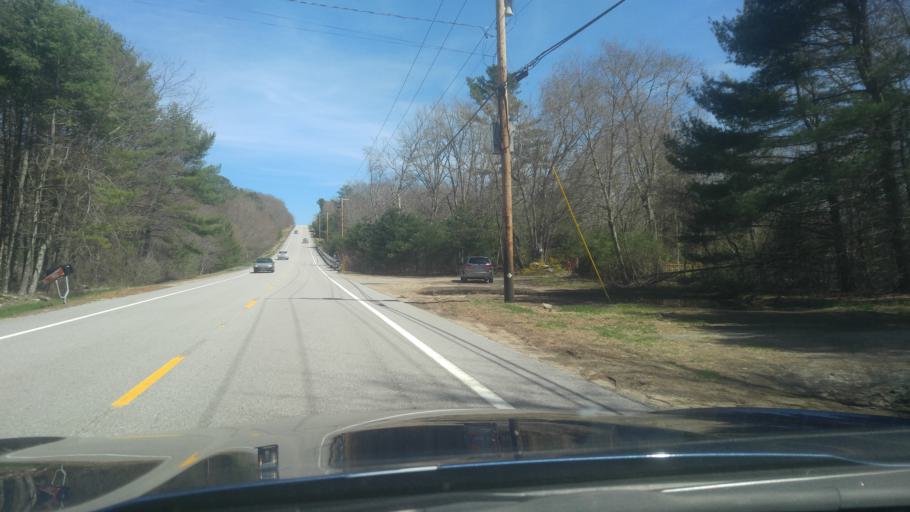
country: US
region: Rhode Island
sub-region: Washington County
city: Hope Valley
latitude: 41.5755
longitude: -71.7459
